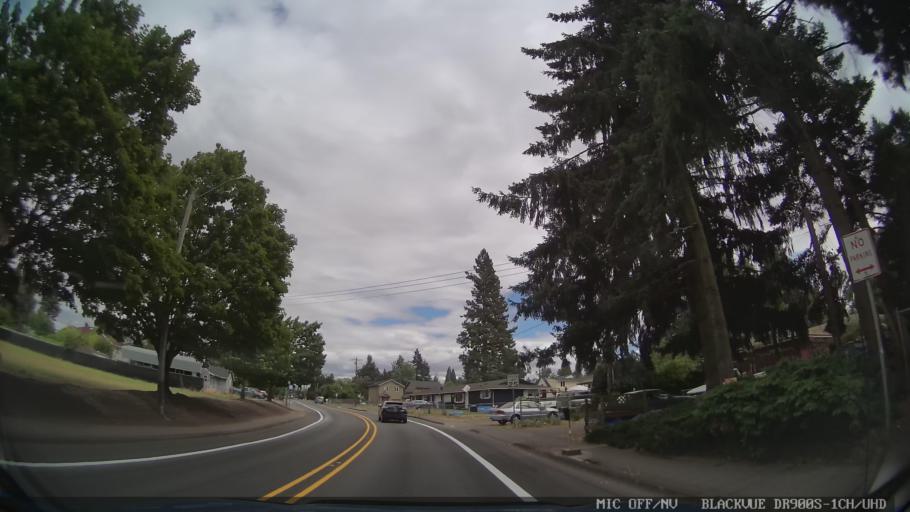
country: US
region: Oregon
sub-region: Marion County
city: Salem
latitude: 44.9541
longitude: -123.0044
